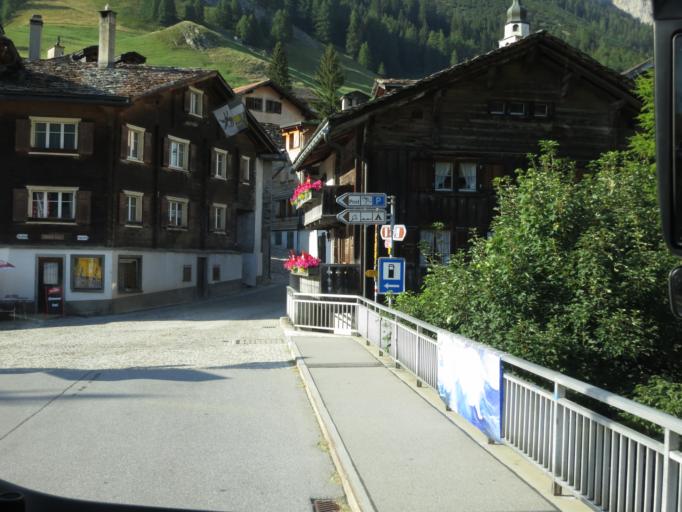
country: CH
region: Grisons
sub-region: Hinterrhein District
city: Hinterrhein
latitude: 46.5526
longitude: 9.3234
